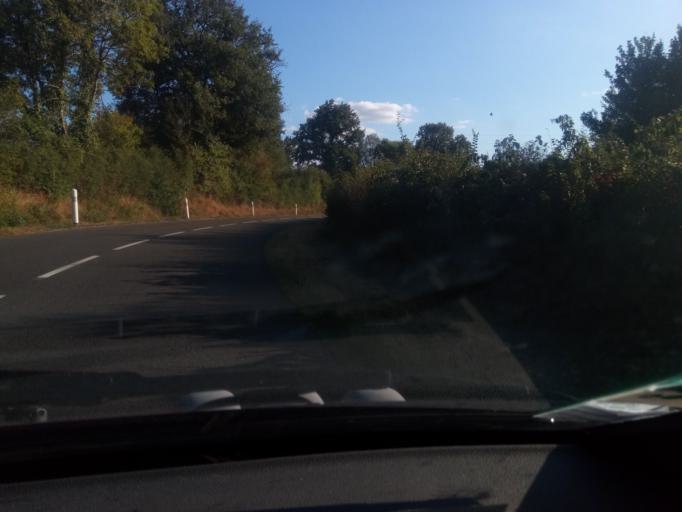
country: FR
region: Poitou-Charentes
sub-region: Departement de la Vienne
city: Availles-Limouzine
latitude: 46.2445
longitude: 0.6911
